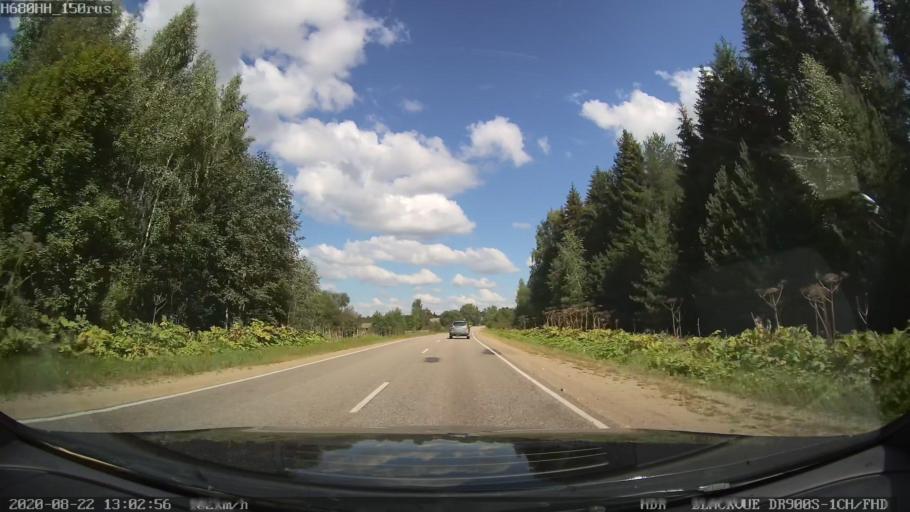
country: RU
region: Tverskaya
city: Bezhetsk
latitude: 57.6556
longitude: 36.4043
